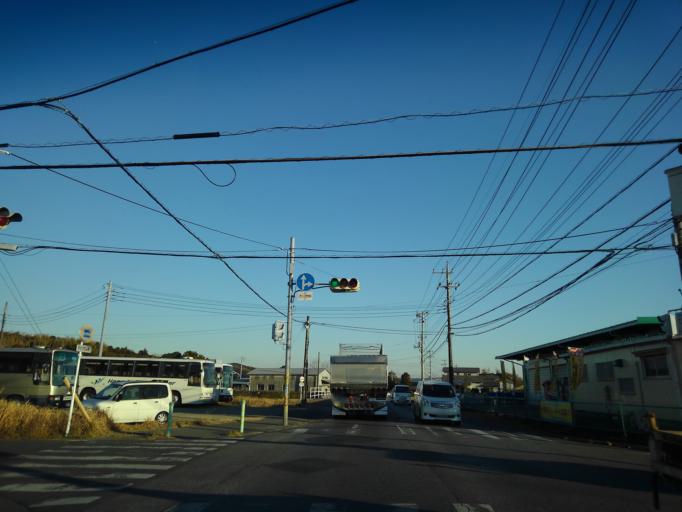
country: JP
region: Chiba
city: Kimitsu
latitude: 35.3183
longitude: 139.9282
